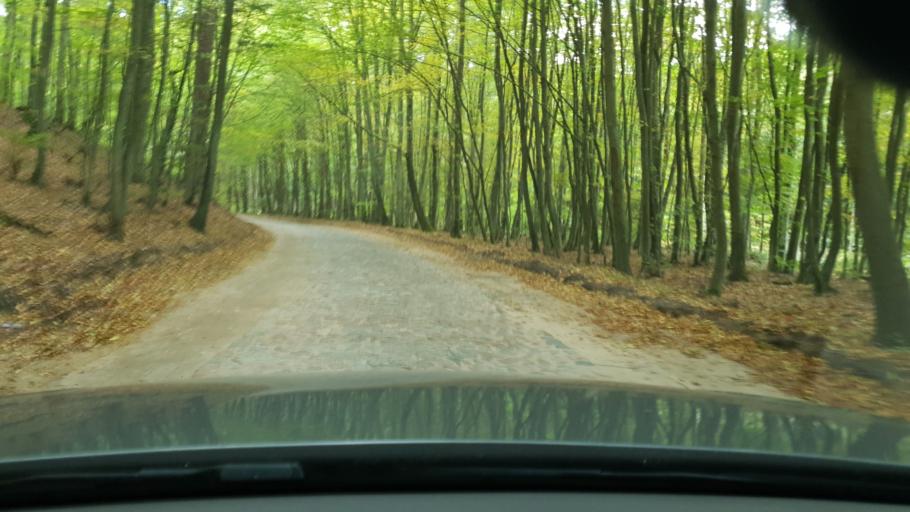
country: PL
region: Pomeranian Voivodeship
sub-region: Powiat wejherowski
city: Reda
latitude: 54.5894
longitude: 18.3279
